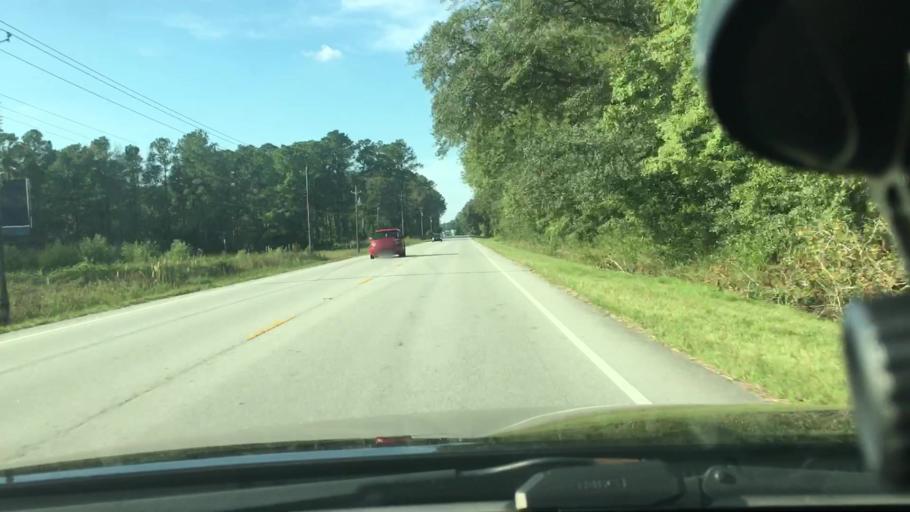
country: US
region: North Carolina
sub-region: Craven County
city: New Bern
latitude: 35.2112
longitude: -77.0616
